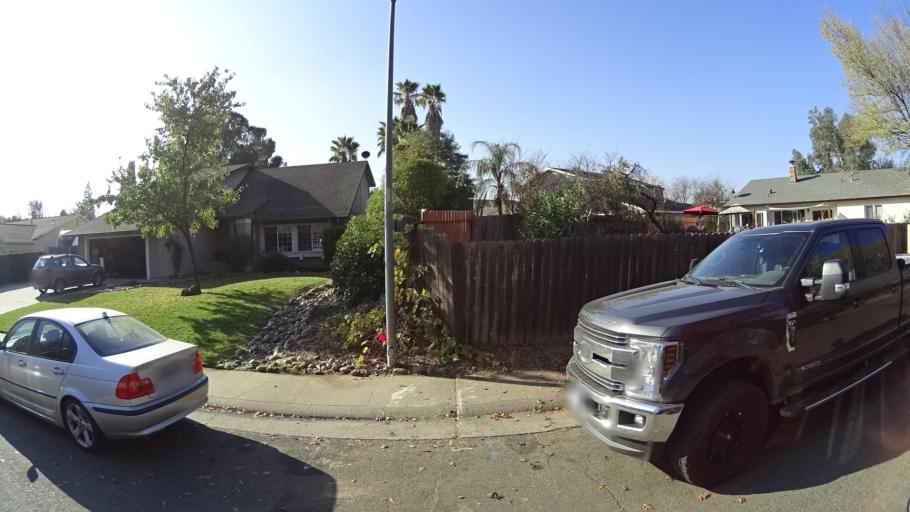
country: US
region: California
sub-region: Sacramento County
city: Citrus Heights
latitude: 38.7172
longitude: -121.2612
